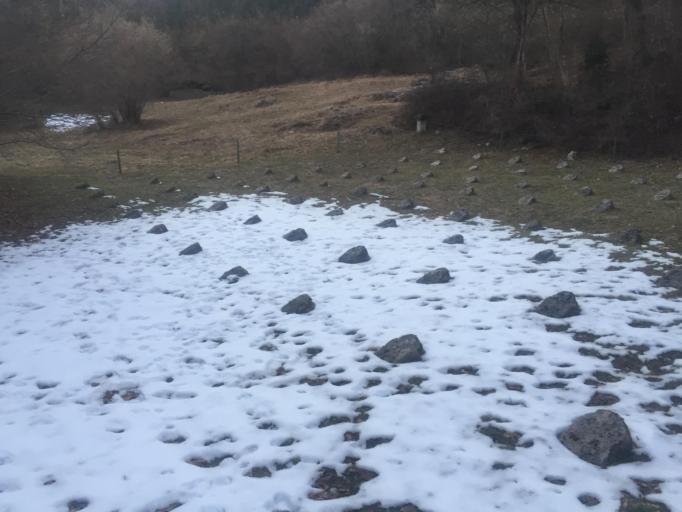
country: SI
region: Kanal
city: Kanal
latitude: 46.0695
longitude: 13.6919
